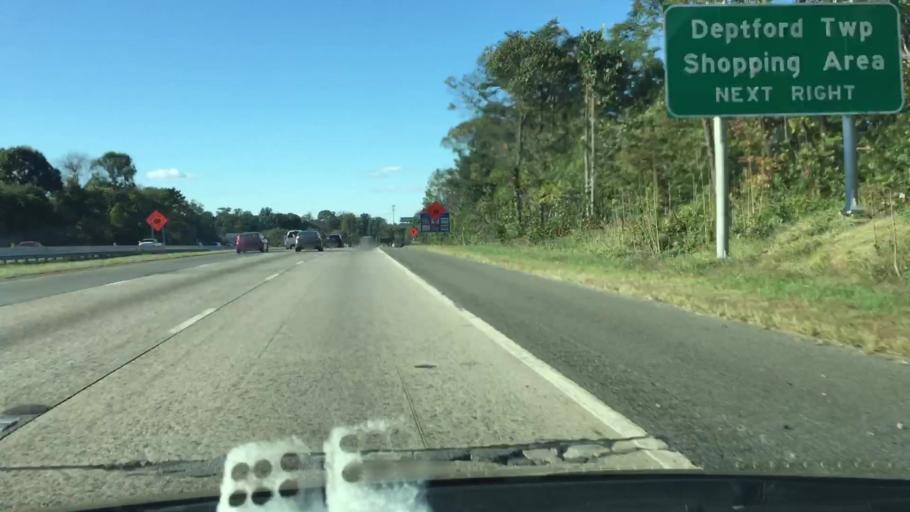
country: US
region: New Jersey
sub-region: Camden County
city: Glendora
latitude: 39.8223
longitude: -75.0784
